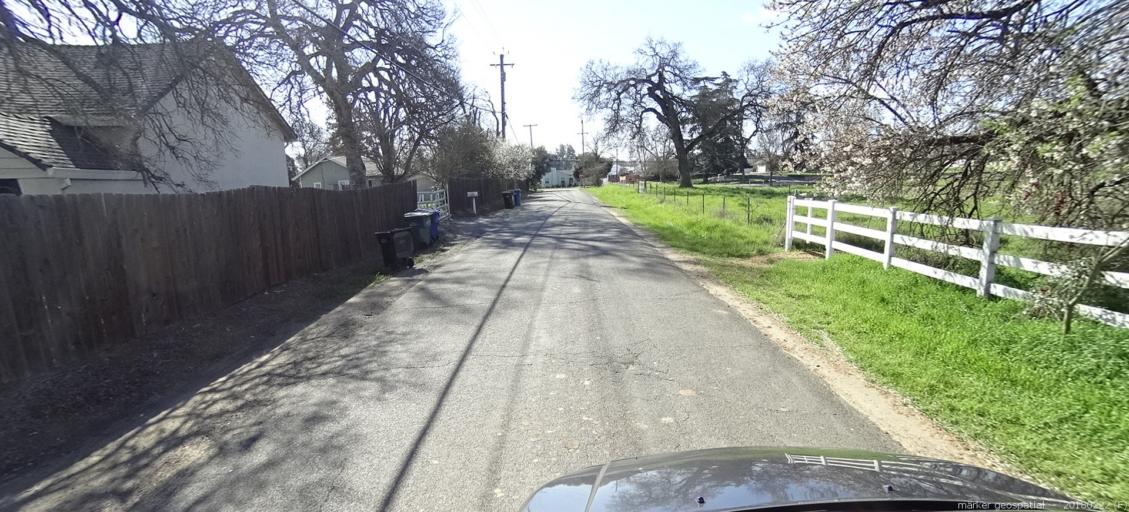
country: US
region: California
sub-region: Sacramento County
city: Rio Linda
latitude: 38.6991
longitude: -121.4337
